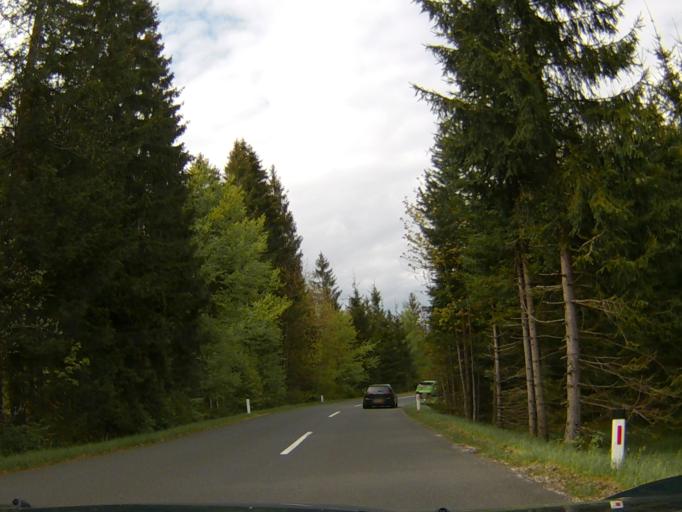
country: AT
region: Carinthia
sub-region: Villach Stadt
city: Villach
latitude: 46.5848
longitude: 13.7997
